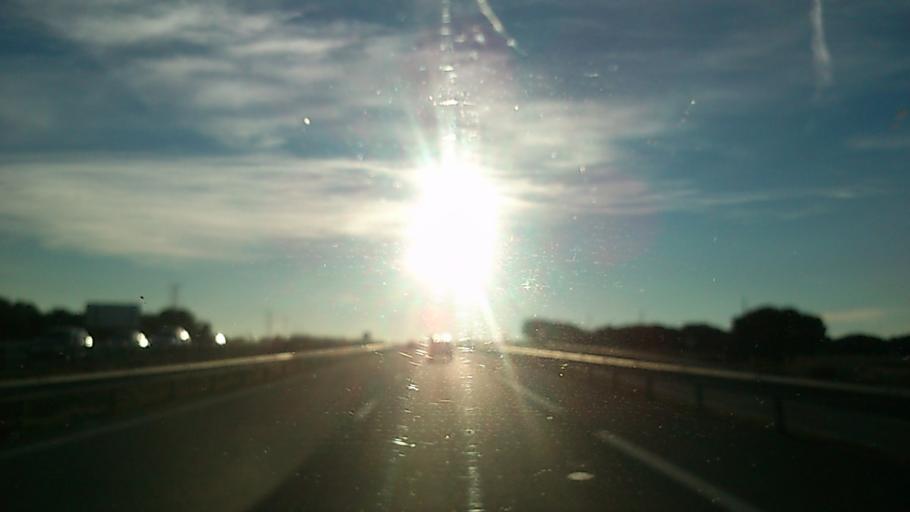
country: ES
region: Castille-La Mancha
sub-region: Provincia de Guadalajara
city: Gajanejos
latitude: 40.8306
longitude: -2.9094
